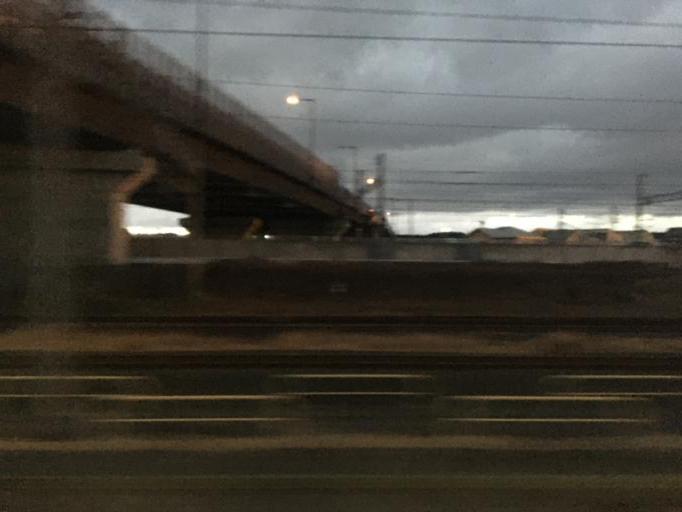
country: JP
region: Aomori
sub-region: Hachinohe Shi
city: Uchimaru
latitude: 40.5145
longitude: 141.4368
